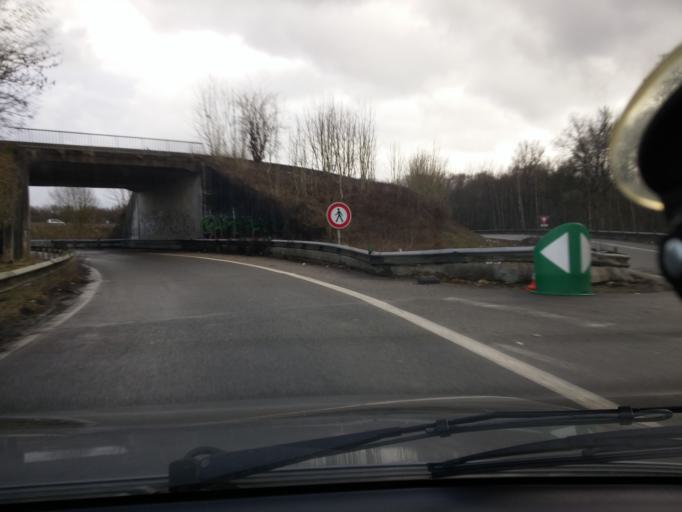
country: FR
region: Ile-de-France
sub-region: Departement de Seine-et-Marne
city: Pontault-Combault
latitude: 48.7739
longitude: 2.6097
